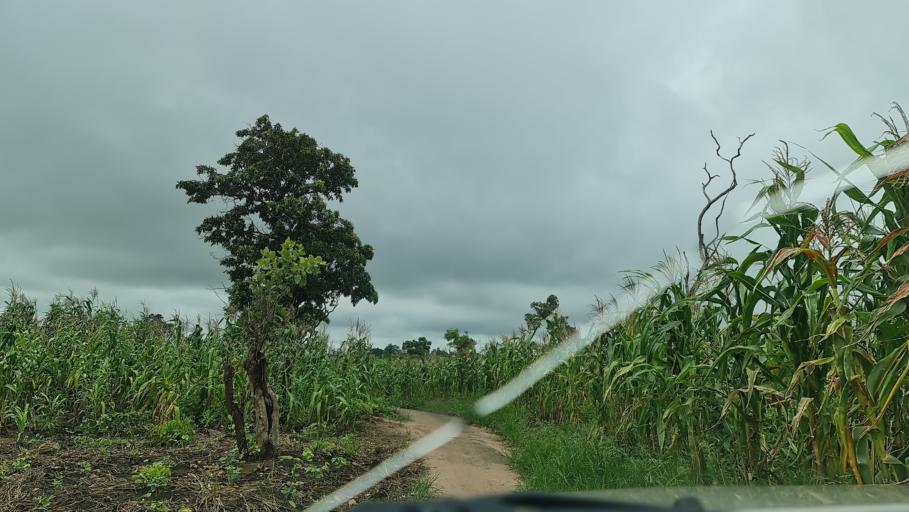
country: MW
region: Southern Region
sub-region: Nsanje District
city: Nsanje
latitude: -17.3395
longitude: 35.7238
